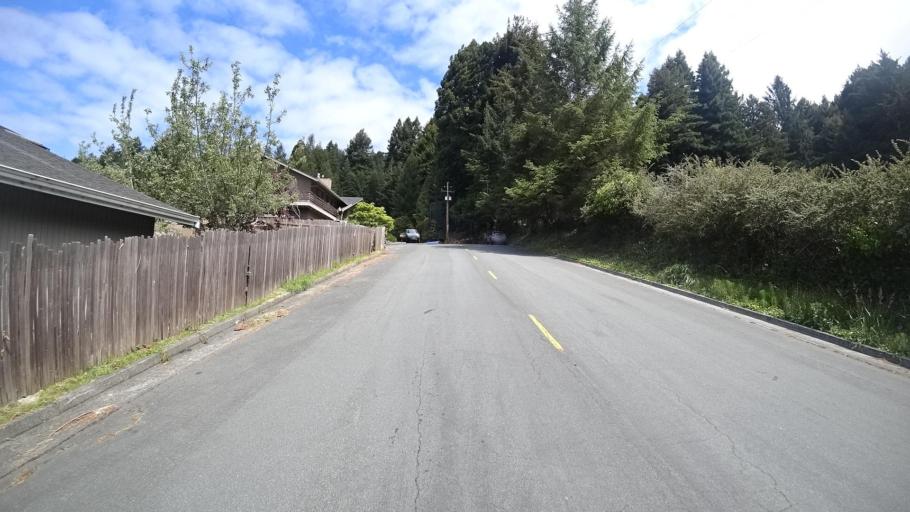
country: US
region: California
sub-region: Humboldt County
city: Bayside
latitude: 40.8575
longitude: -124.0580
